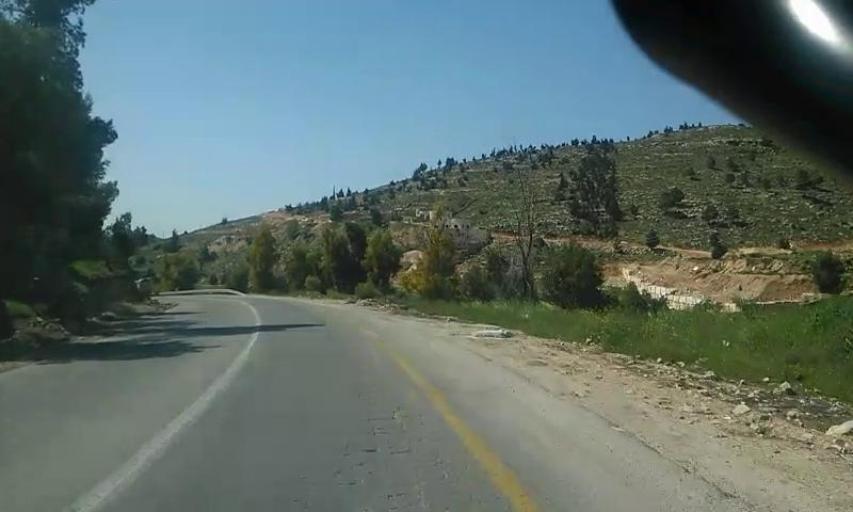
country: PS
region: West Bank
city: Ar Rihiyah
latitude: 31.4904
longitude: 35.0664
